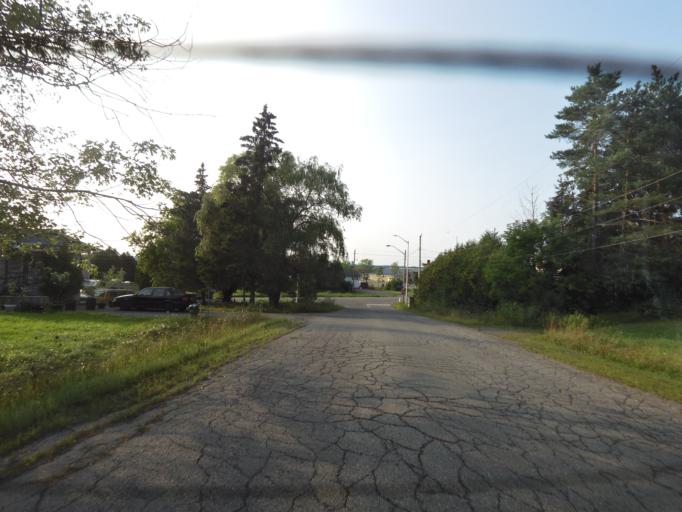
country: CA
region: Ontario
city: Clarence-Rockland
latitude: 45.4931
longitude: -75.4685
